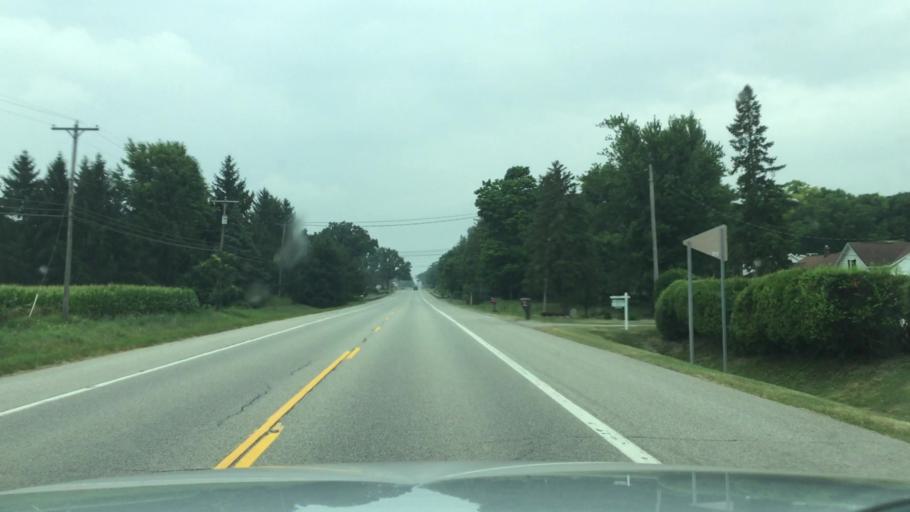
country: US
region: Michigan
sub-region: Shiawassee County
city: New Haven
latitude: 43.0532
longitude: -84.1772
